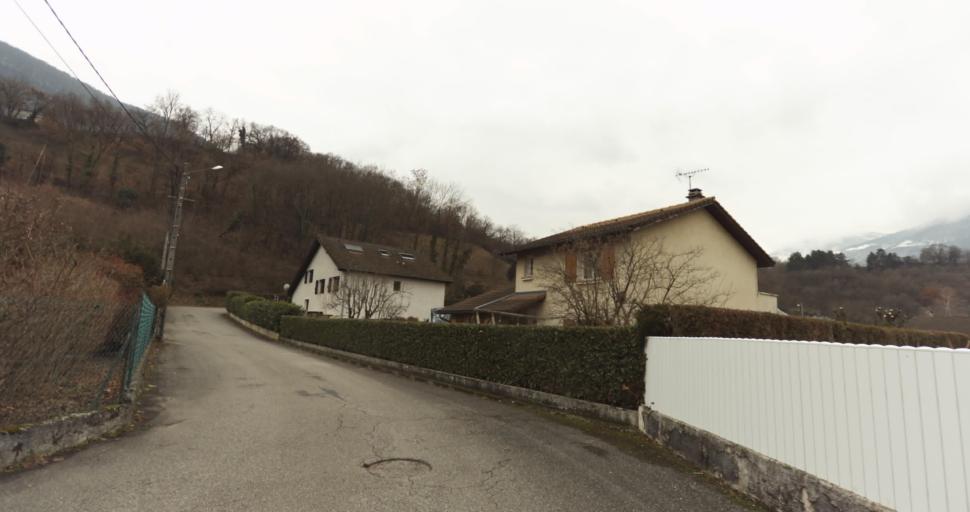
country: FR
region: Rhone-Alpes
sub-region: Departement de l'Isere
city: Vif
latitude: 45.0494
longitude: 5.6790
